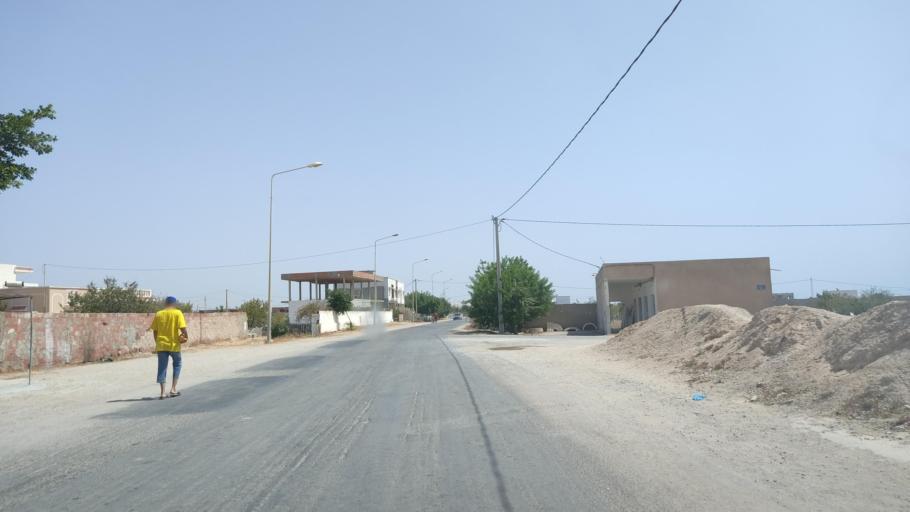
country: TN
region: Safaqis
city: Sfax
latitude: 34.6745
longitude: 10.7168
